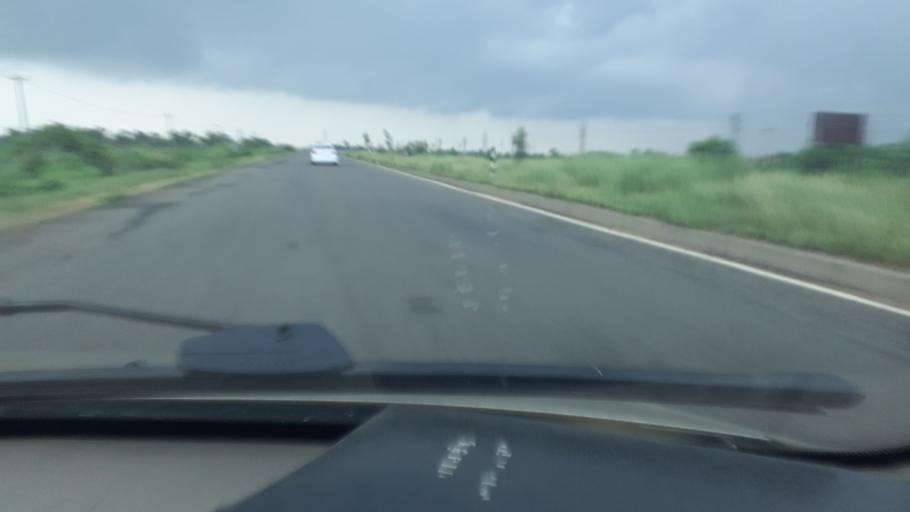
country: IN
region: Tamil Nadu
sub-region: Thoothukkudi
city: Kovilpatti
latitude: 9.1090
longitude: 77.8102
